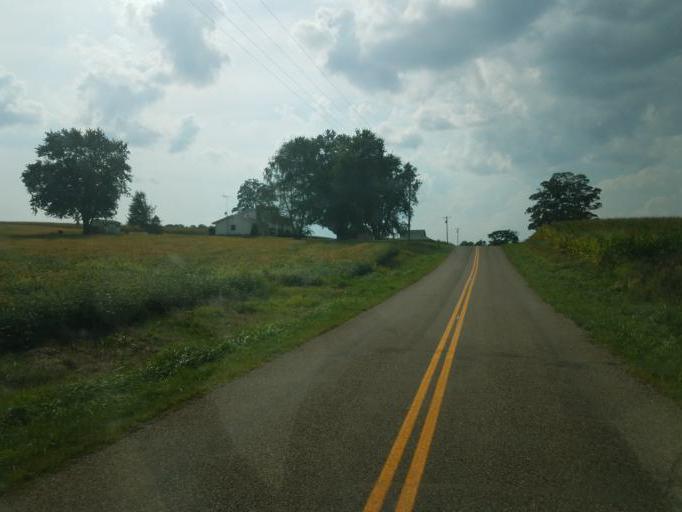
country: US
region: Ohio
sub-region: Knox County
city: Gambier
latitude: 40.3367
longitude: -82.3690
